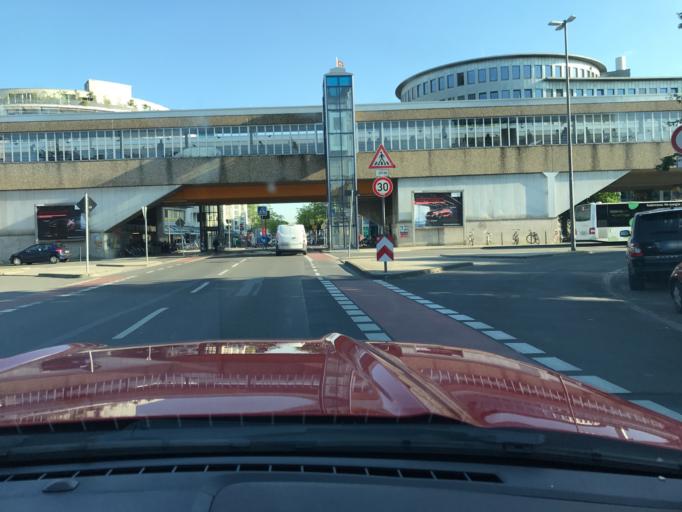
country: DE
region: North Rhine-Westphalia
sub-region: Regierungsbezirk Koln
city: Nippes
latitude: 50.9718
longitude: 6.9516
